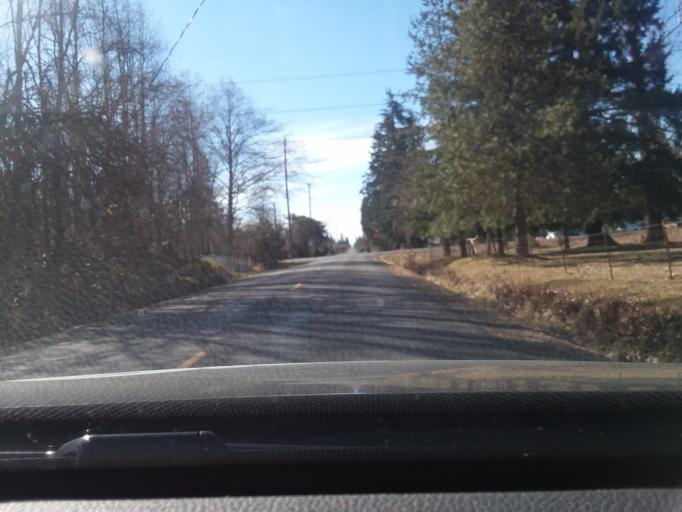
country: US
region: Washington
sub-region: Pierce County
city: Waller
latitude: 47.1816
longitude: -122.3785
